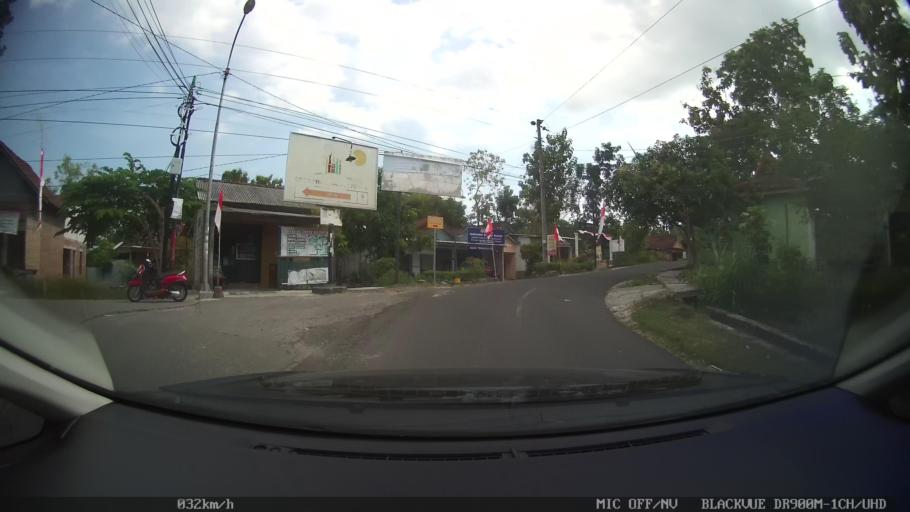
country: ID
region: Daerah Istimewa Yogyakarta
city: Kasihan
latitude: -7.8539
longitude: 110.3125
